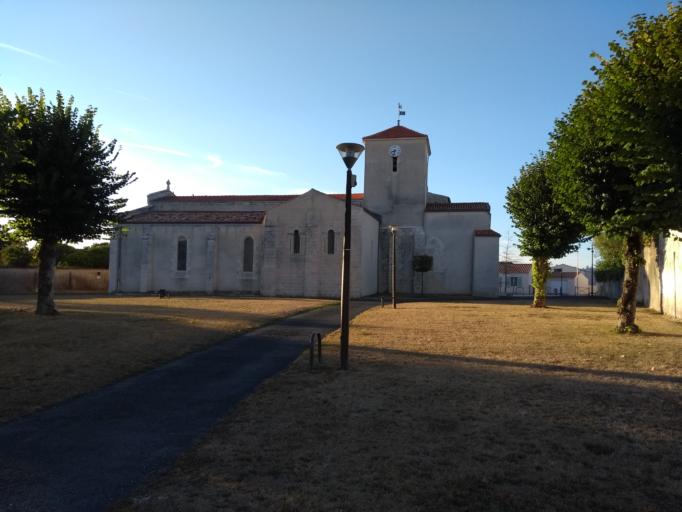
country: FR
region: Poitou-Charentes
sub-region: Departement de la Charente-Maritime
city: Andilly
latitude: 46.2536
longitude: -1.0282
